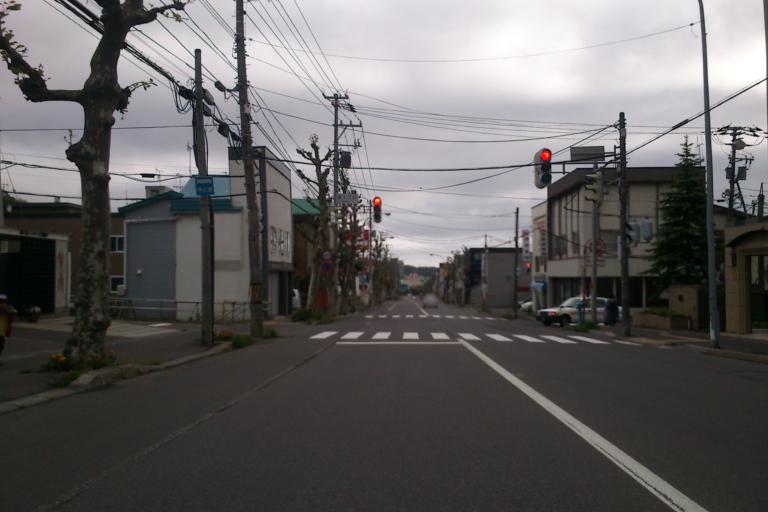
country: JP
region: Hokkaido
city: Otaru
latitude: 43.1898
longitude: 140.9901
